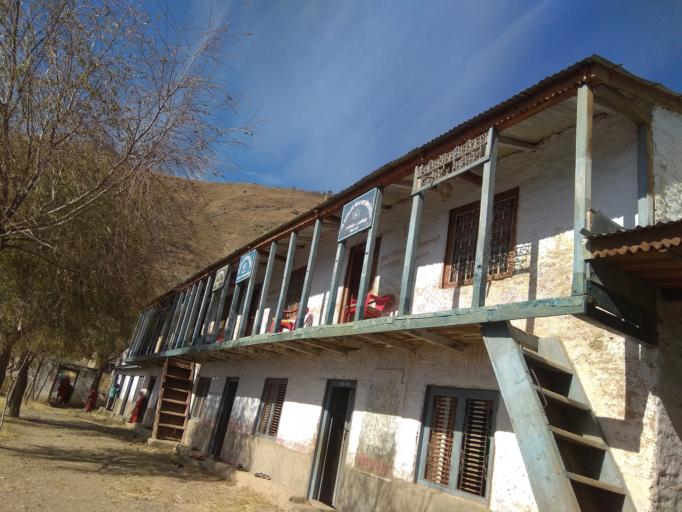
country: NP
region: Mid Western
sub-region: Bheri Zone
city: Dailekh
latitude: 29.2961
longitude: 81.7192
